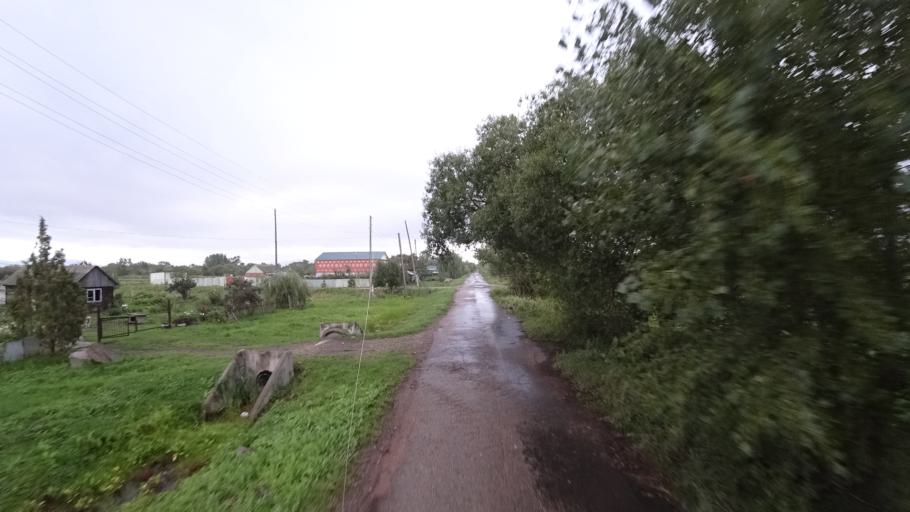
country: RU
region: Primorskiy
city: Chernigovka
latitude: 44.4083
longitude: 132.5326
